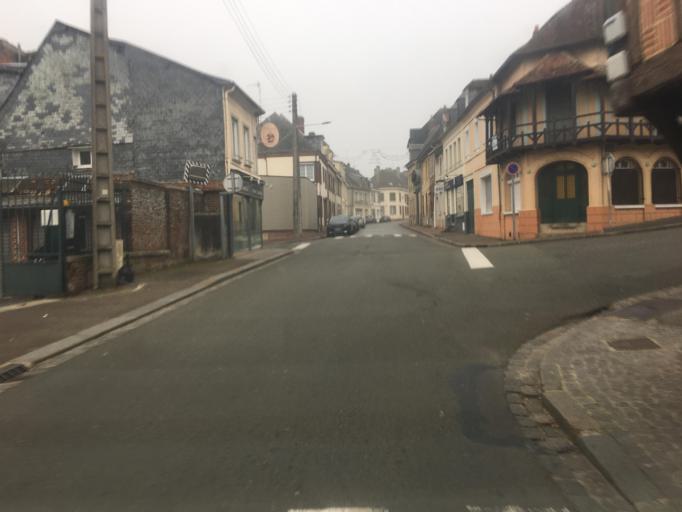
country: FR
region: Haute-Normandie
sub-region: Departement de la Seine-Maritime
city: Neufchatel-en-Bray
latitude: 49.7323
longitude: 1.4458
